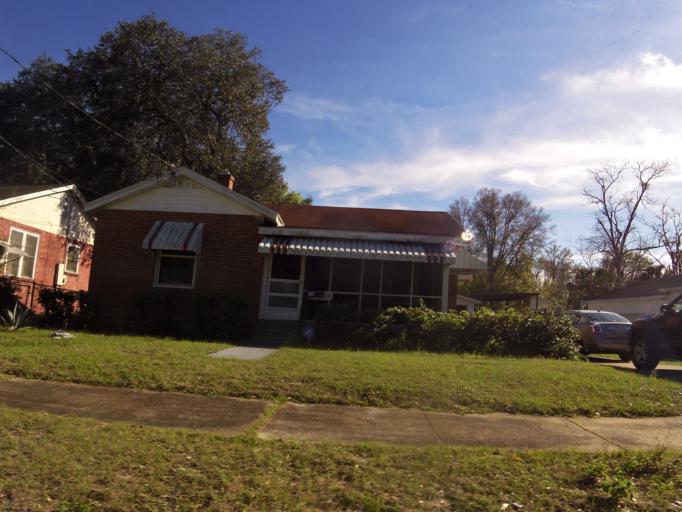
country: US
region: Florida
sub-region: Duval County
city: Jacksonville
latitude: 30.3784
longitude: -81.6484
